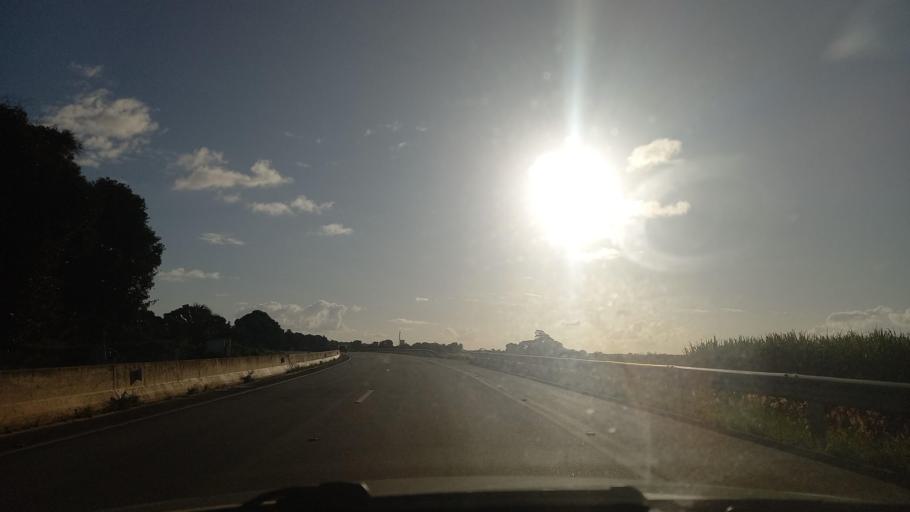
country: BR
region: Alagoas
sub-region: Campo Alegre
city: Campo Alegre
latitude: -9.8036
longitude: -36.2665
